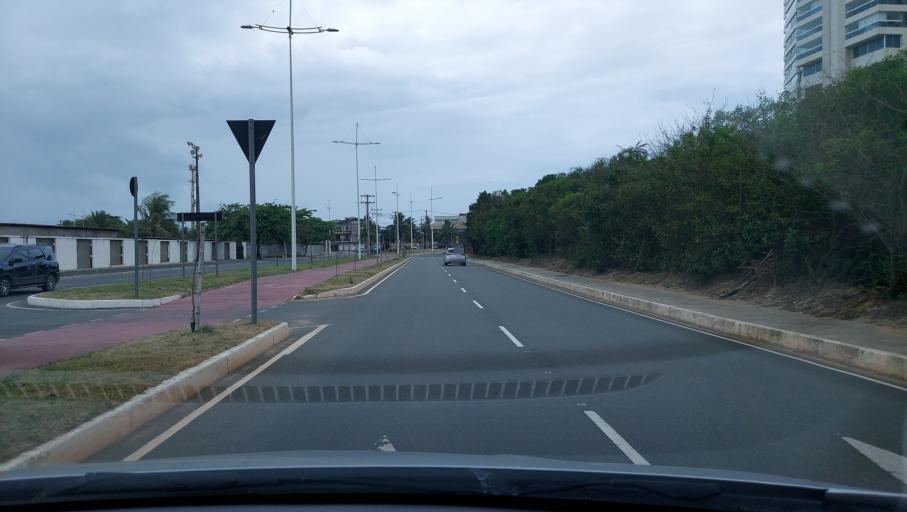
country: BR
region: Bahia
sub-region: Lauro De Freitas
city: Lauro de Freitas
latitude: -12.9610
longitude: -38.4027
